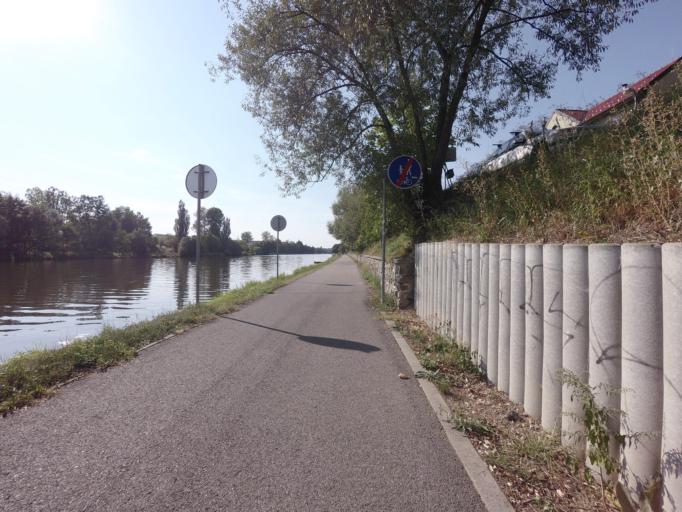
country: CZ
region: Jihocesky
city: Tyn nad Vltavou
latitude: 49.2158
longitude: 14.4361
